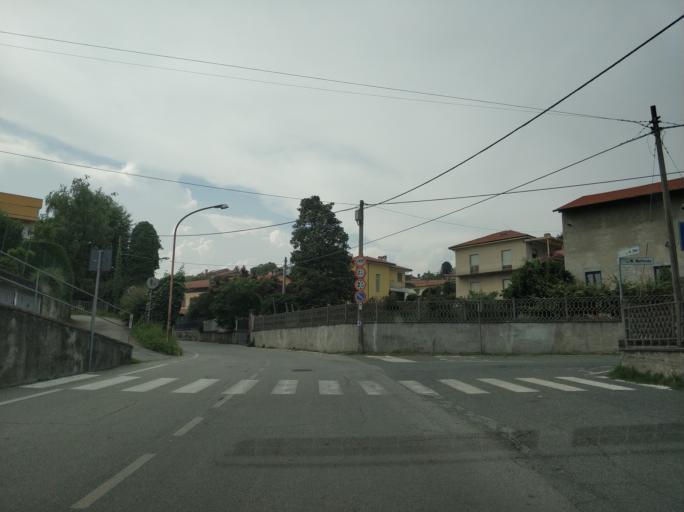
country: IT
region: Piedmont
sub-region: Provincia di Torino
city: Caluso
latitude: 45.3063
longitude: 7.8977
